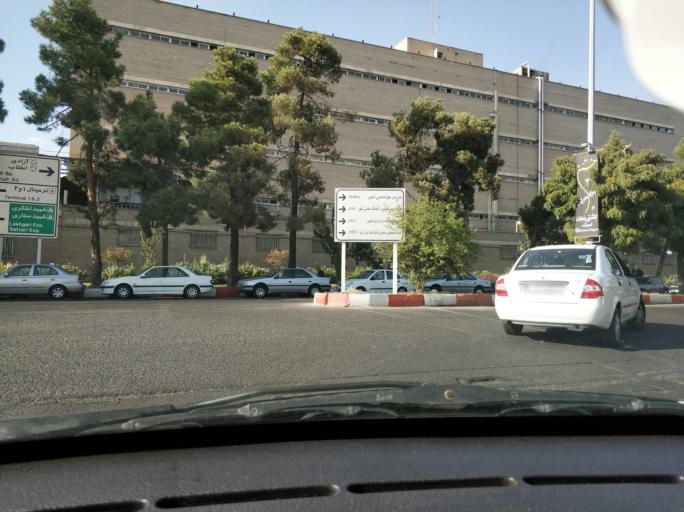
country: IR
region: Tehran
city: Tehran
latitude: 35.6959
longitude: 51.3292
